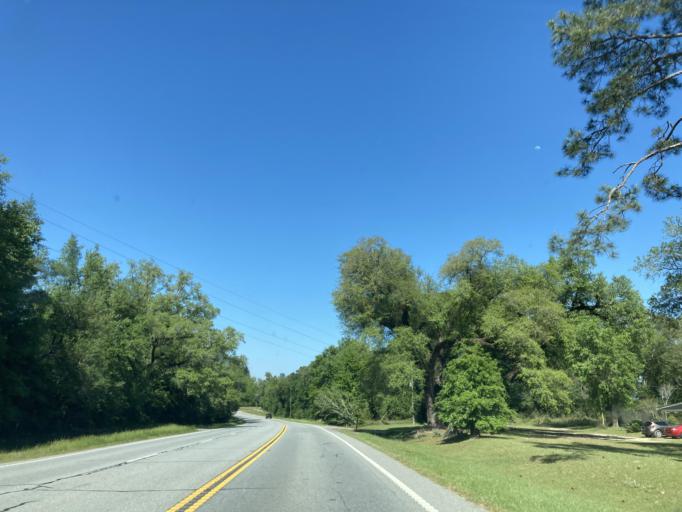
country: US
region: Georgia
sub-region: Baker County
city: Newton
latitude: 31.2928
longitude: -84.3516
